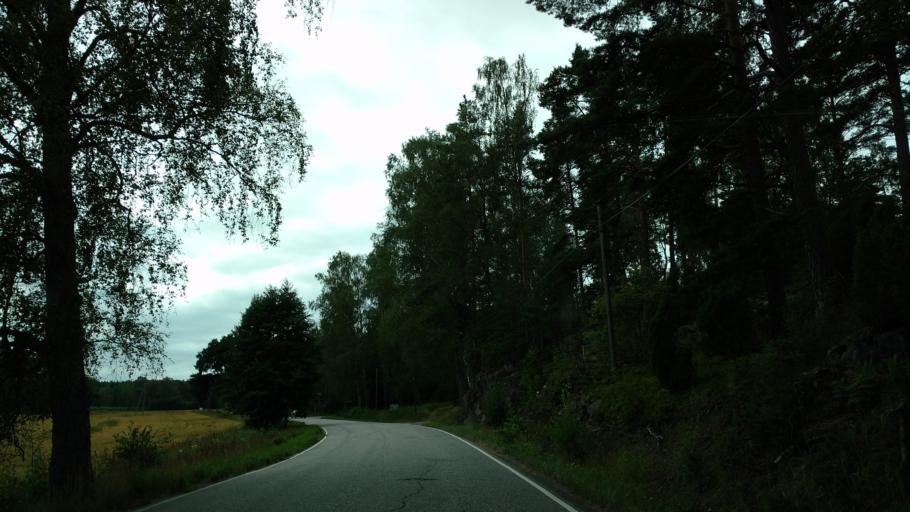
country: FI
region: Varsinais-Suomi
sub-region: Aboland-Turunmaa
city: Dragsfjaerd
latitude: 60.0379
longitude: 22.4424
